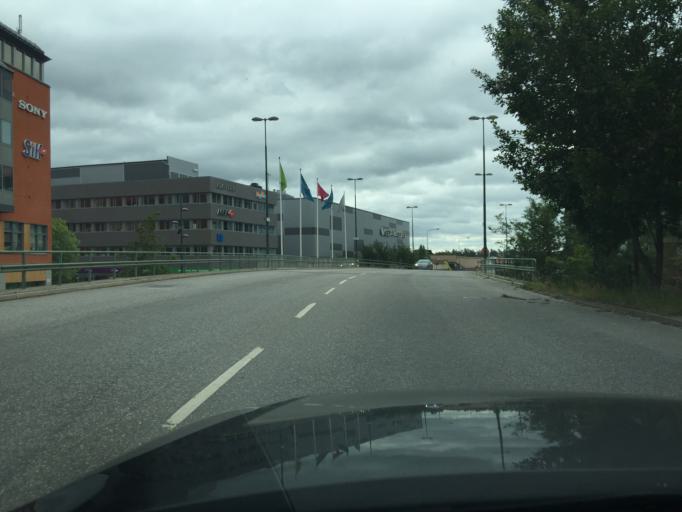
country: SE
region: Stockholm
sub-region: Stockholms Kommun
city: Kista
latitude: 59.4064
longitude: 17.9544
